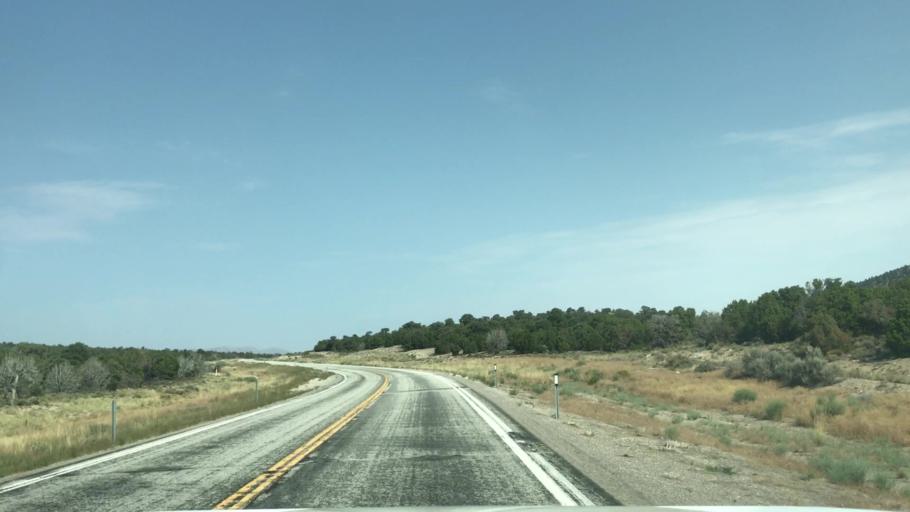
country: US
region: Nevada
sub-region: White Pine County
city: McGill
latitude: 39.1363
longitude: -114.3281
